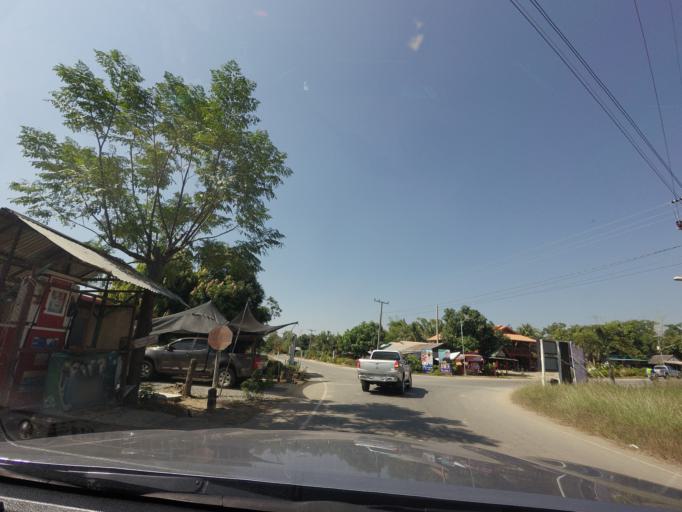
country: TH
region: Sukhothai
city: Si Samrong
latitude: 17.1315
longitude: 99.7779
